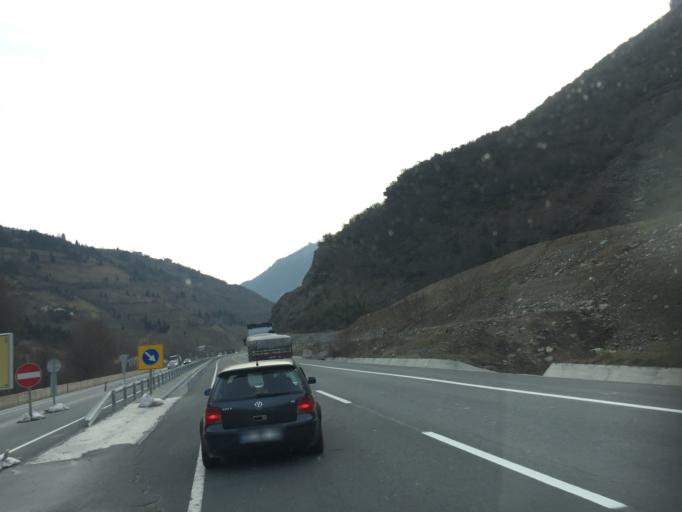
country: TR
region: Trabzon
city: Macka
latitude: 40.7916
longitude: 39.5811
